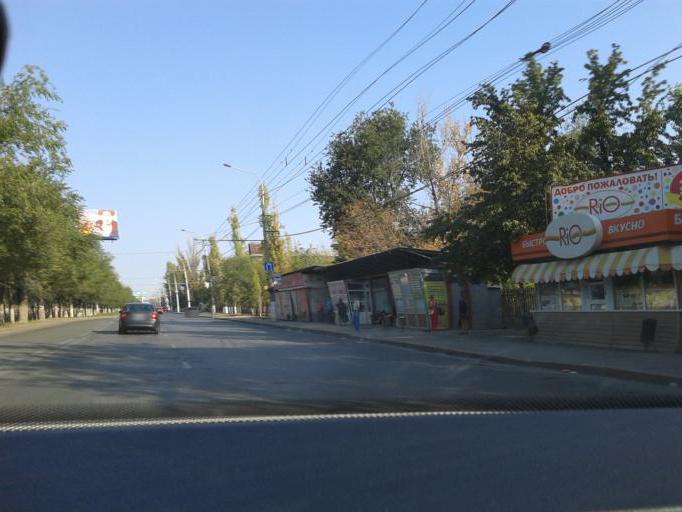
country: RU
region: Volgograd
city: Volgograd
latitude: 48.7358
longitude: 44.4944
